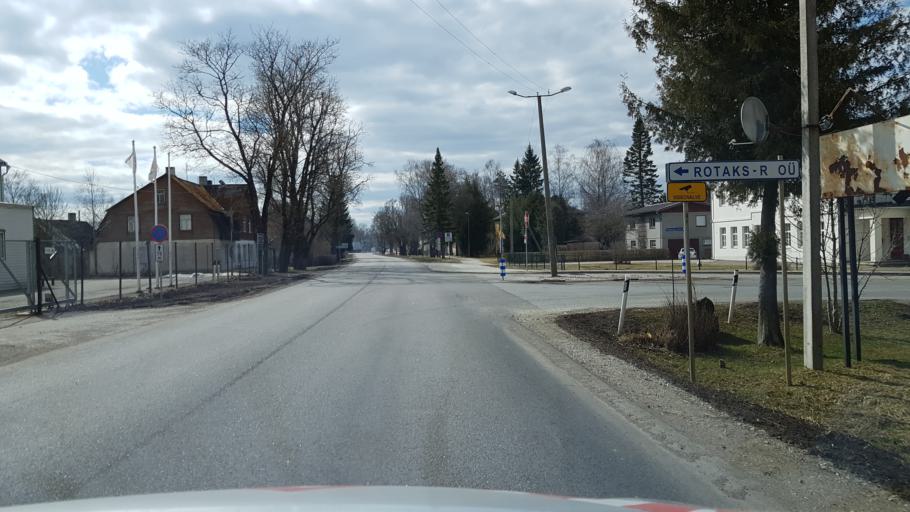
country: EE
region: Laeaene-Virumaa
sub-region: Vaeike-Maarja vald
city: Vaike-Maarja
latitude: 59.1328
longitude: 26.2554
